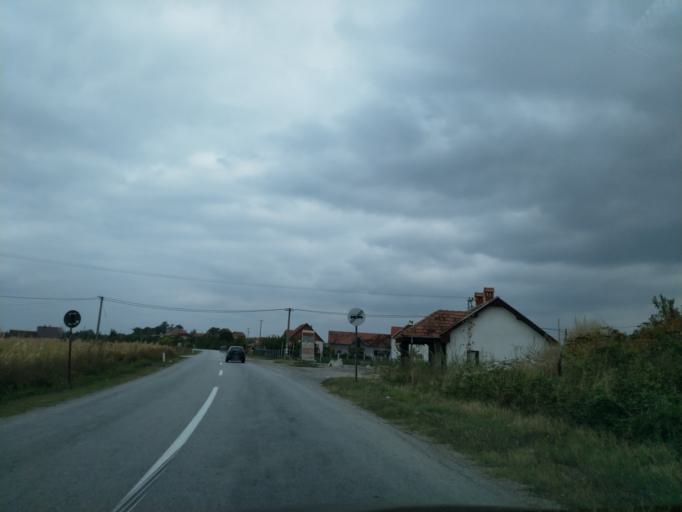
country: RS
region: Central Serbia
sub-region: Sumadijski Okrug
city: Topola
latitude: 44.1815
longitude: 20.7399
